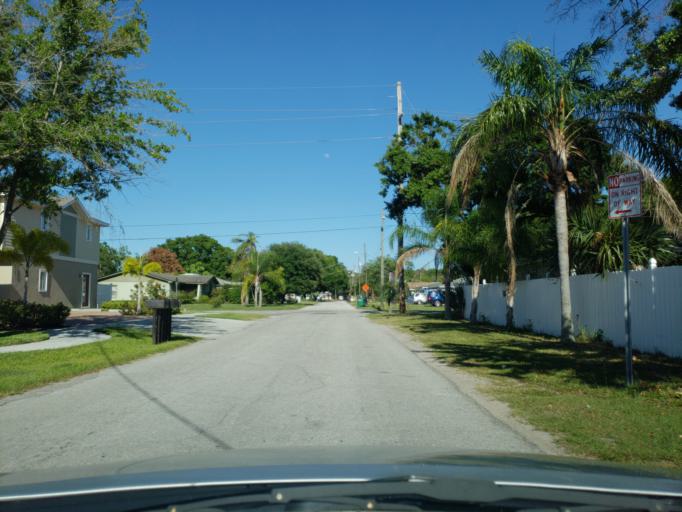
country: US
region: Florida
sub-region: Hillsborough County
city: Tampa
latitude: 27.9494
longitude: -82.5041
